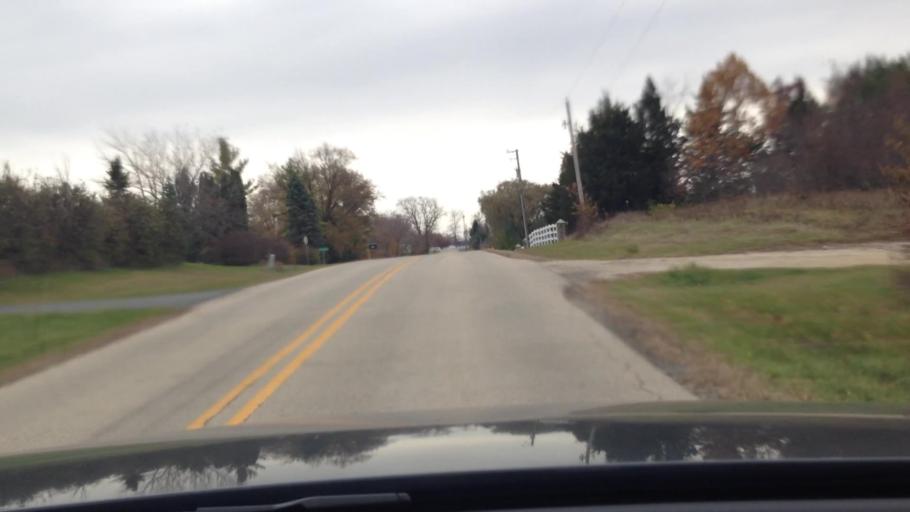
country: US
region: Illinois
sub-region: McHenry County
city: Woodstock
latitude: 42.2799
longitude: -88.4770
